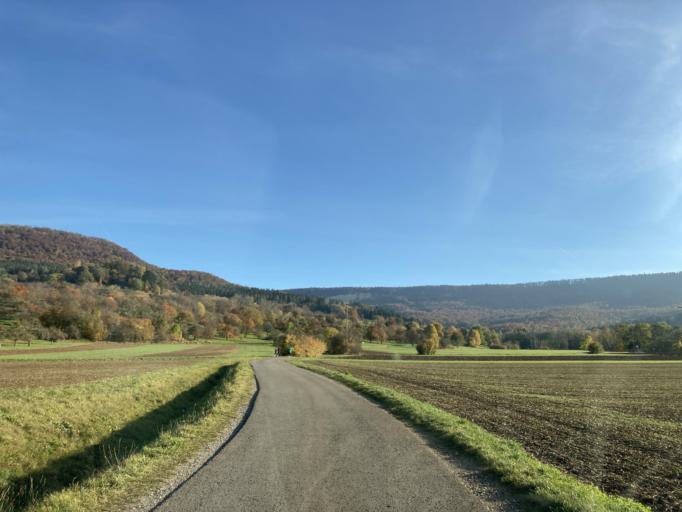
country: DE
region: Baden-Wuerttemberg
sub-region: Tuebingen Region
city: Mossingen
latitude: 48.3954
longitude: 9.0501
